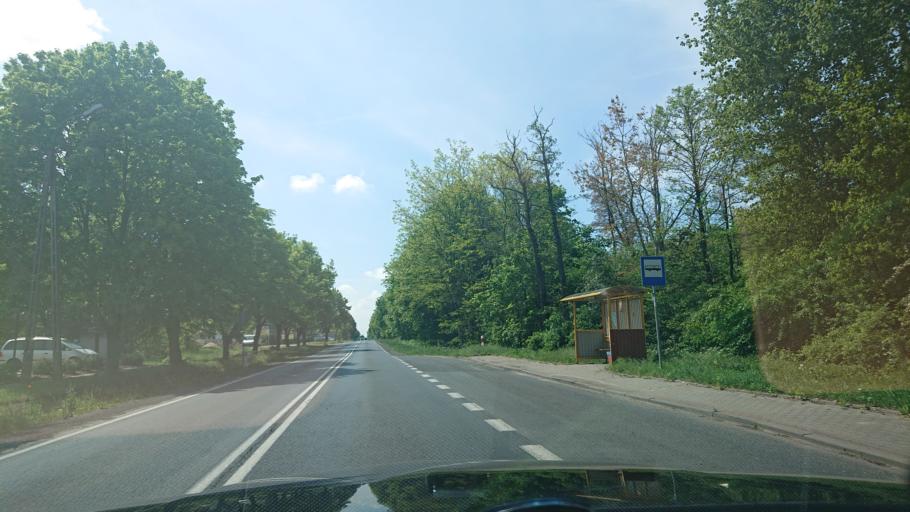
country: PL
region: Greater Poland Voivodeship
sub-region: Powiat gnieznienski
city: Gniezno
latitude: 52.4826
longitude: 17.5933
